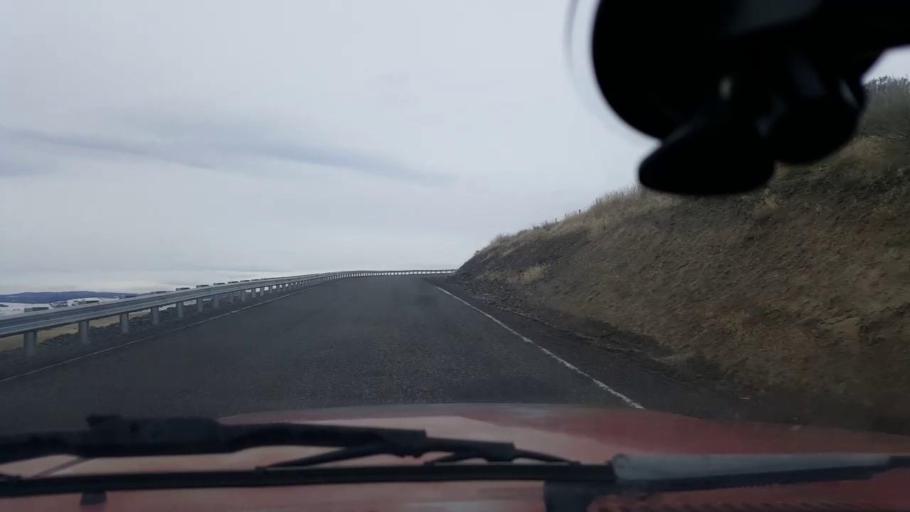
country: US
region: Washington
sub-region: Asotin County
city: Clarkston Heights-Vineland
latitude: 46.3206
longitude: -117.3498
